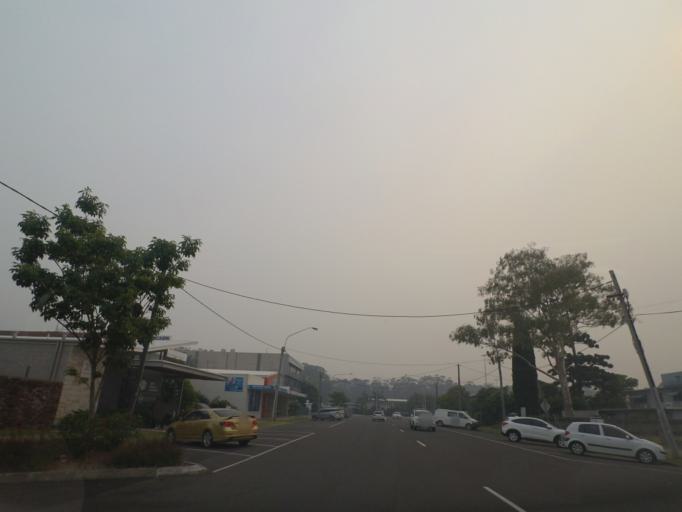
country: AU
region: New South Wales
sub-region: Coffs Harbour
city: Coffs Harbour
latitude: -30.2965
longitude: 153.1177
